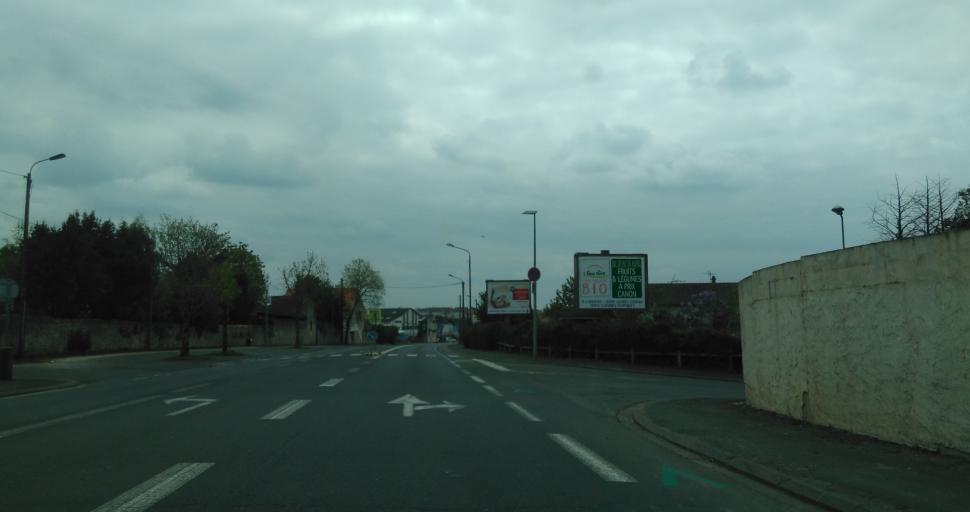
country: FR
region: Poitou-Charentes
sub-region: Departement des Deux-Sevres
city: Niort
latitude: 46.3428
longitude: -0.4447
